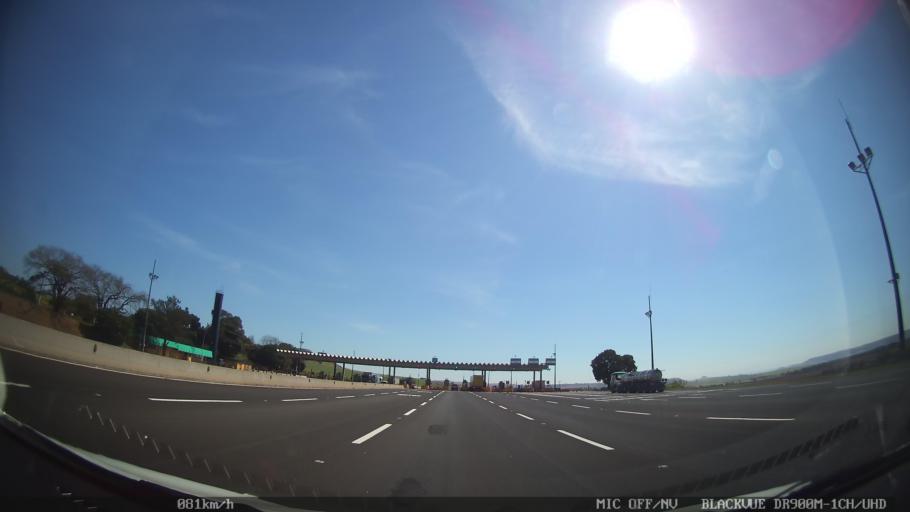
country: BR
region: Sao Paulo
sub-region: Cravinhos
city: Cravinhos
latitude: -21.4149
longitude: -47.6631
